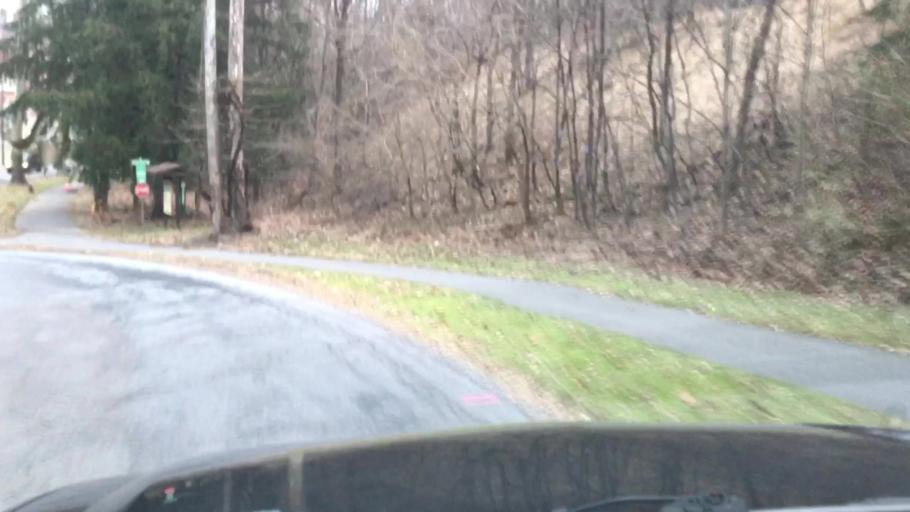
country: US
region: Pennsylvania
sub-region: Dauphin County
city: Harrisburg
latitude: 40.2824
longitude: -76.8724
